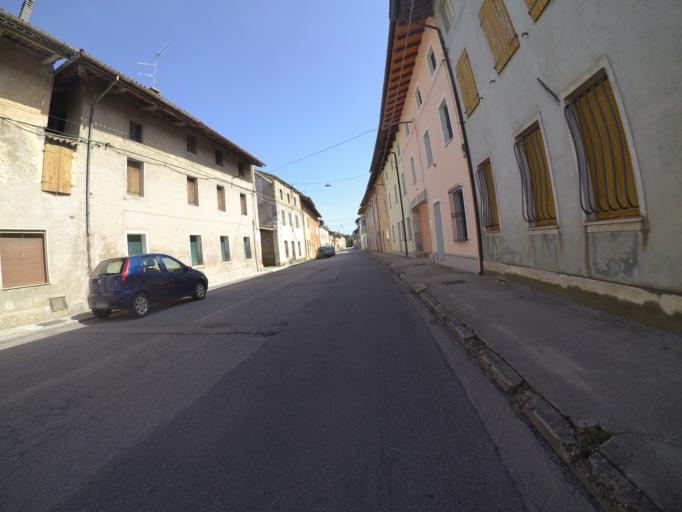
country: IT
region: Friuli Venezia Giulia
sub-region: Provincia di Udine
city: Mortegliano
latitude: 45.9411
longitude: 13.1723
